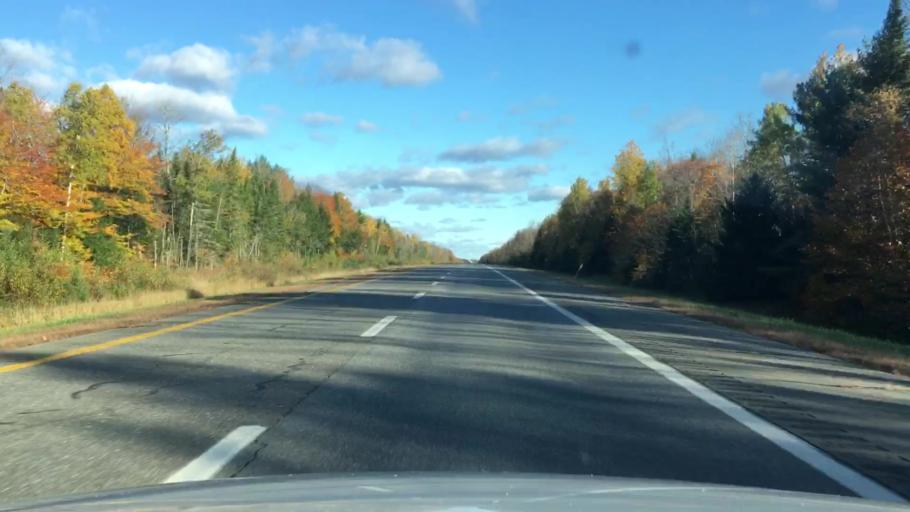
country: US
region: Maine
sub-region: Penobscot County
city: Greenbush
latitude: 45.0771
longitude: -68.6915
